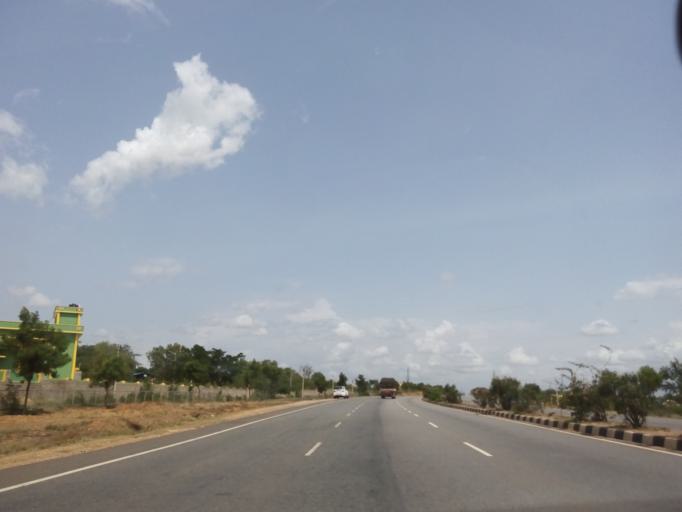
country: IN
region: Karnataka
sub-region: Tumkur
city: Sira
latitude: 13.7497
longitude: 76.8863
